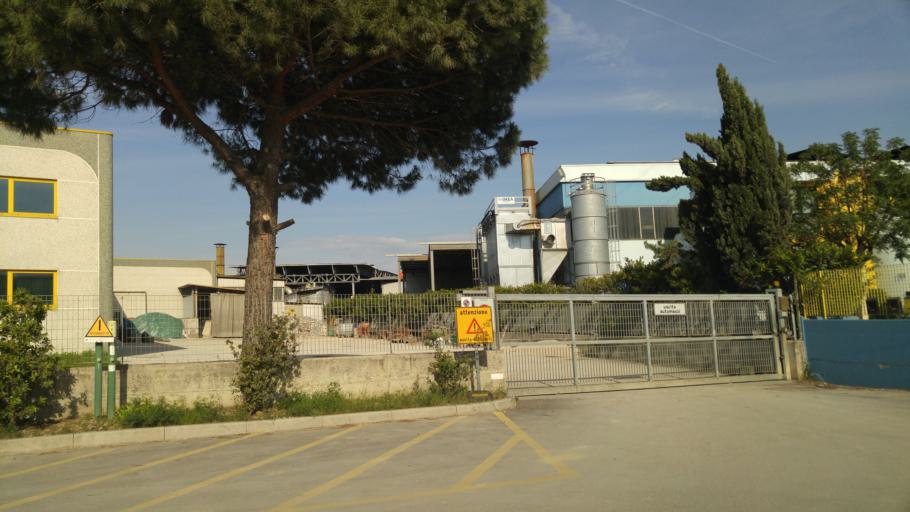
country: IT
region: The Marches
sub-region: Provincia di Pesaro e Urbino
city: Bellocchi
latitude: 43.7934
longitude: 13.0122
